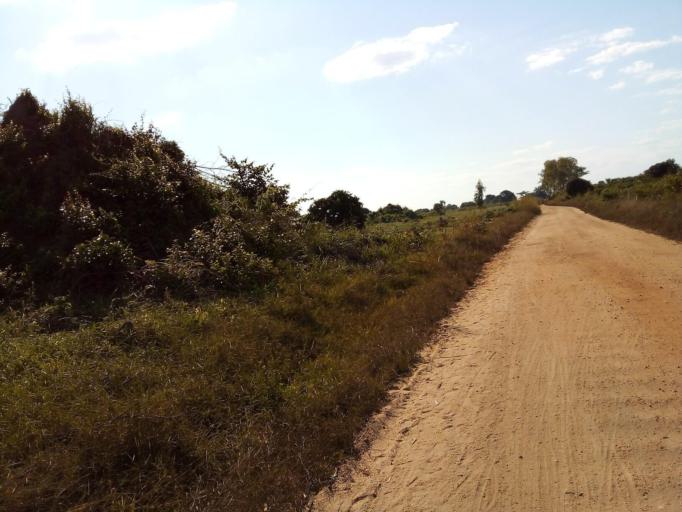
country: MZ
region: Zambezia
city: Quelimane
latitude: -17.5679
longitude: 36.6373
